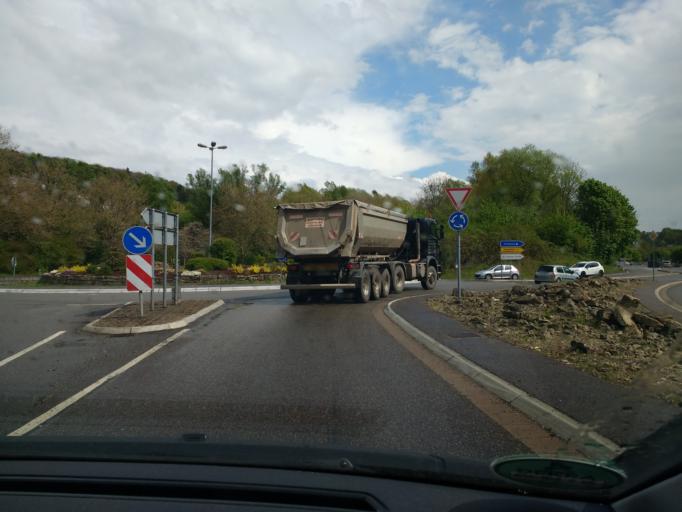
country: DE
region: Saarland
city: Kleinblittersdorf
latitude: 49.1508
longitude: 7.0394
